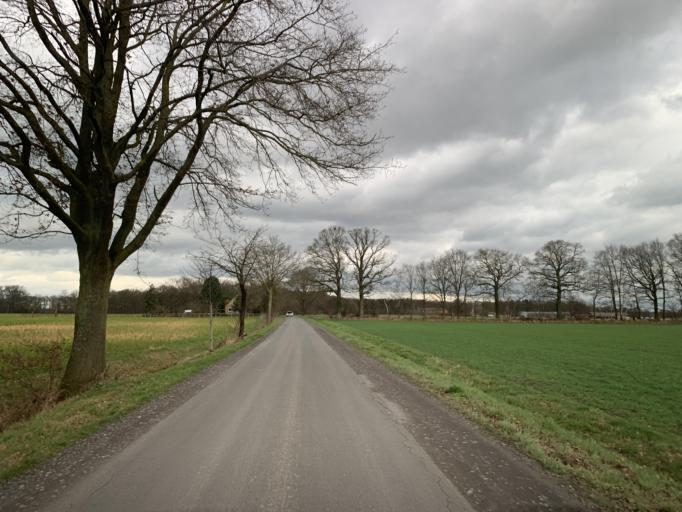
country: DE
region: North Rhine-Westphalia
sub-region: Regierungsbezirk Munster
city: Muenster
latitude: 52.0152
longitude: 7.6381
